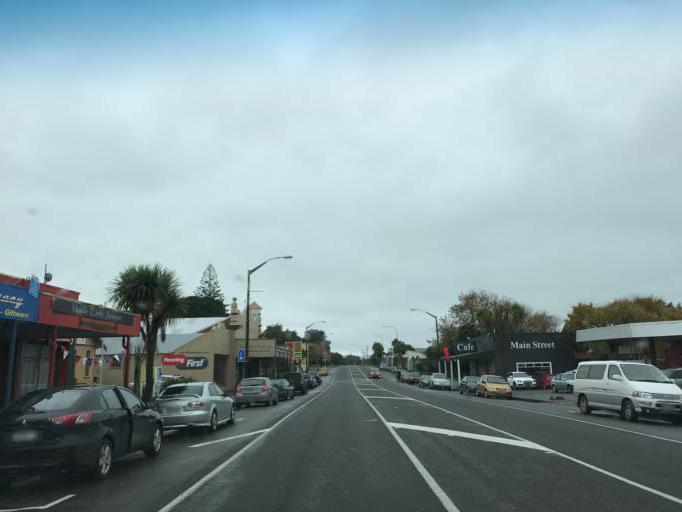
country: NZ
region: Taranaki
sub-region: South Taranaki District
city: Patea
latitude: -39.7640
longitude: 174.6334
